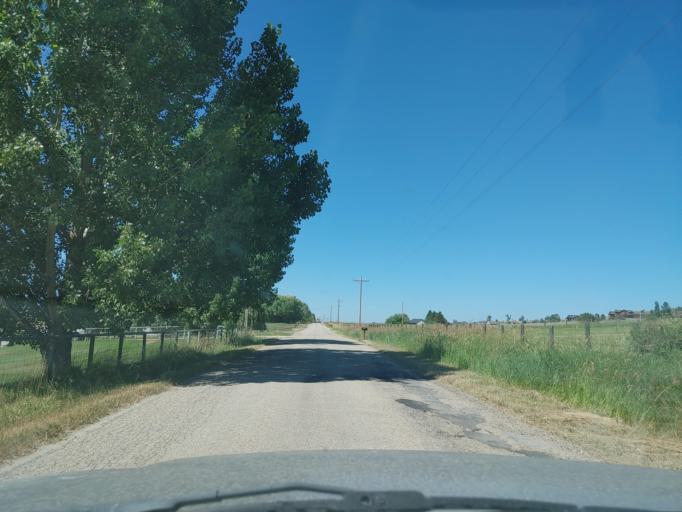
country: US
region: Montana
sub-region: Ravalli County
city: Hamilton
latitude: 46.3408
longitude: -114.0615
